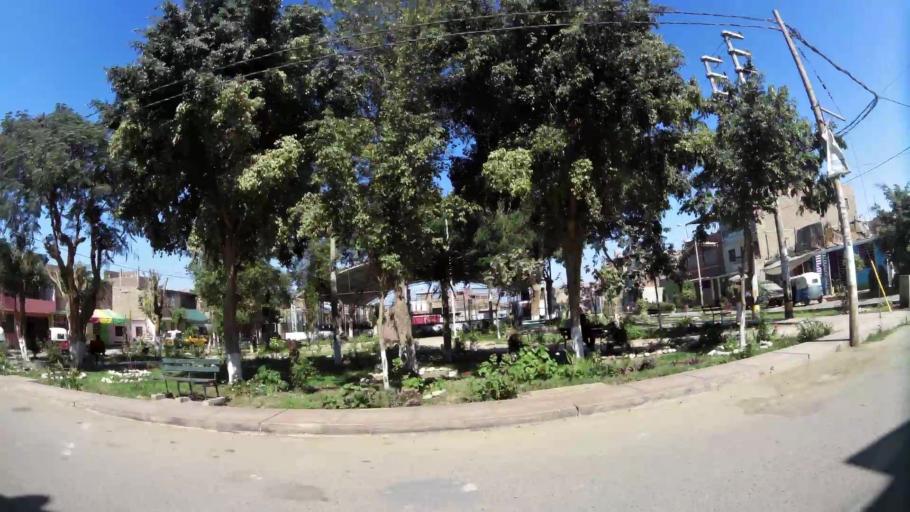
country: PE
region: Ica
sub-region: Provincia de Ica
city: Ica
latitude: -14.0573
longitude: -75.7247
